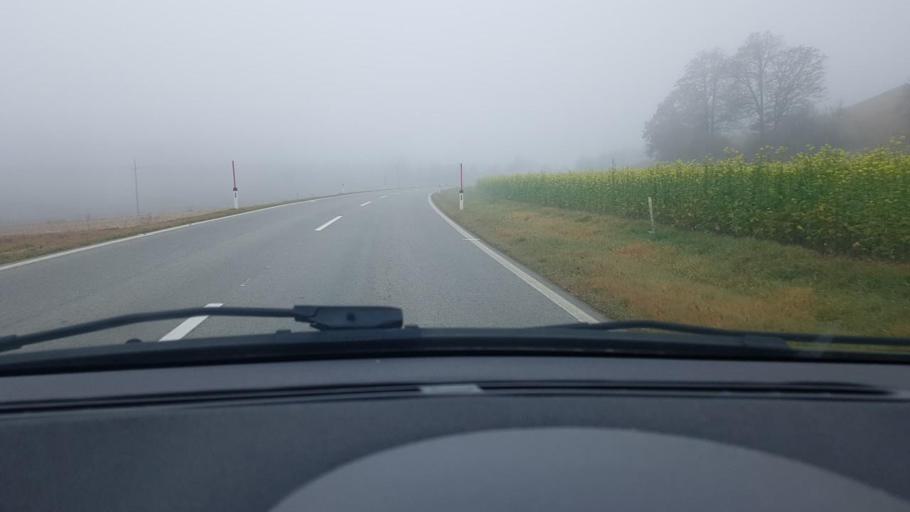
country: AT
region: Carinthia
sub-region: Politischer Bezirk Volkermarkt
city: Eberndorf
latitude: 46.5626
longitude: 14.6638
